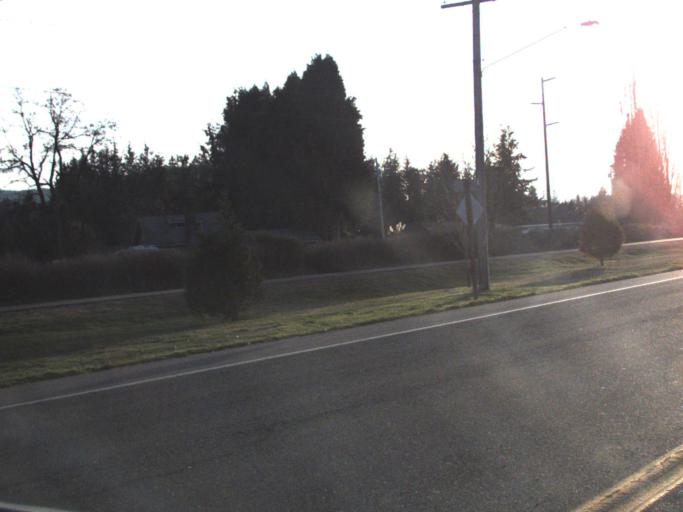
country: US
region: Washington
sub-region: Skagit County
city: Sedro-Woolley
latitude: 48.5135
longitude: -122.2156
